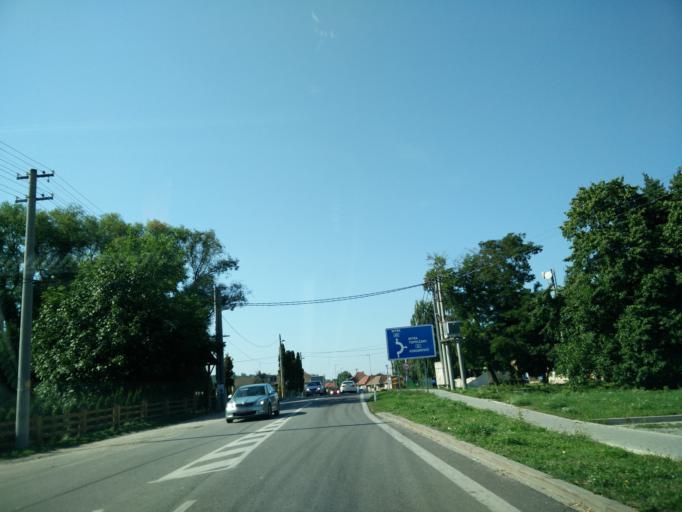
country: SK
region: Nitriansky
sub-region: Okres Nitra
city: Nitra
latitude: 48.4249
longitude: 18.1239
